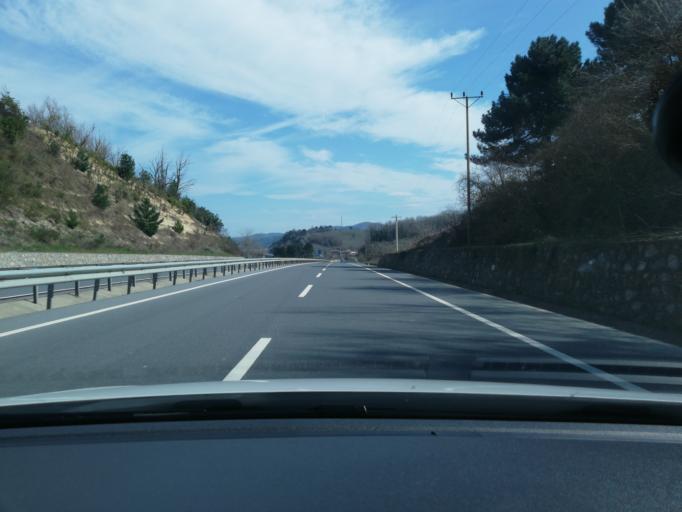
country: TR
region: Duzce
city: Akcakoca
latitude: 41.1018
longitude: 31.2427
